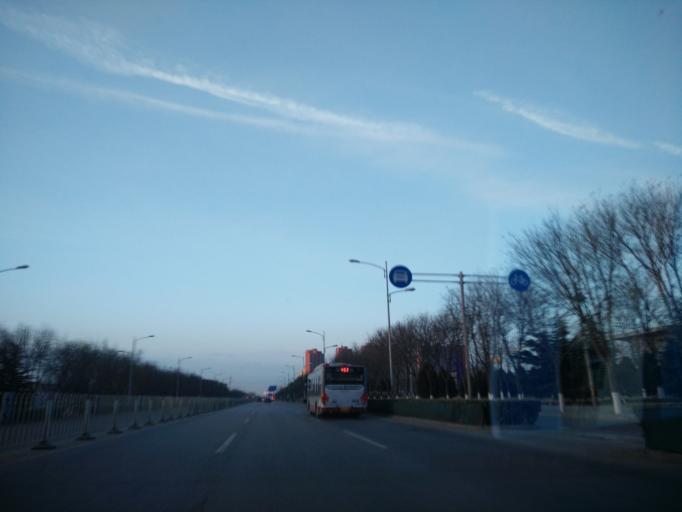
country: CN
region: Beijing
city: Jiugong
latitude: 39.7695
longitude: 116.5097
